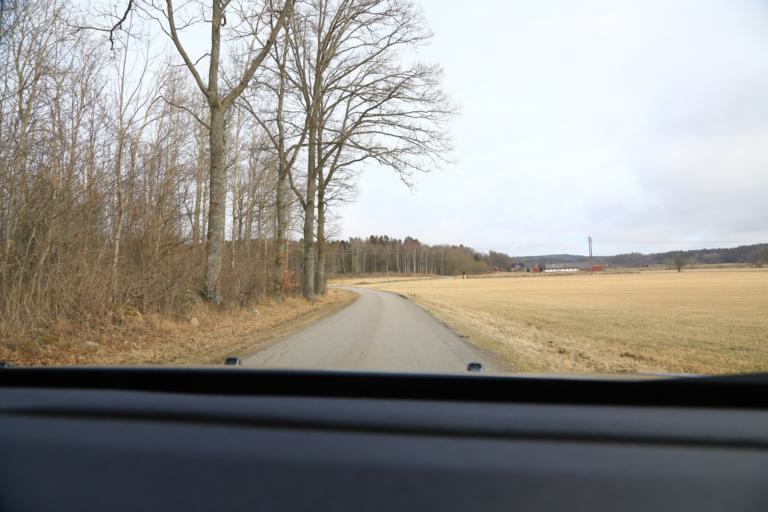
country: SE
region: Halland
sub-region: Varbergs Kommun
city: Veddige
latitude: 57.2132
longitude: 12.2471
